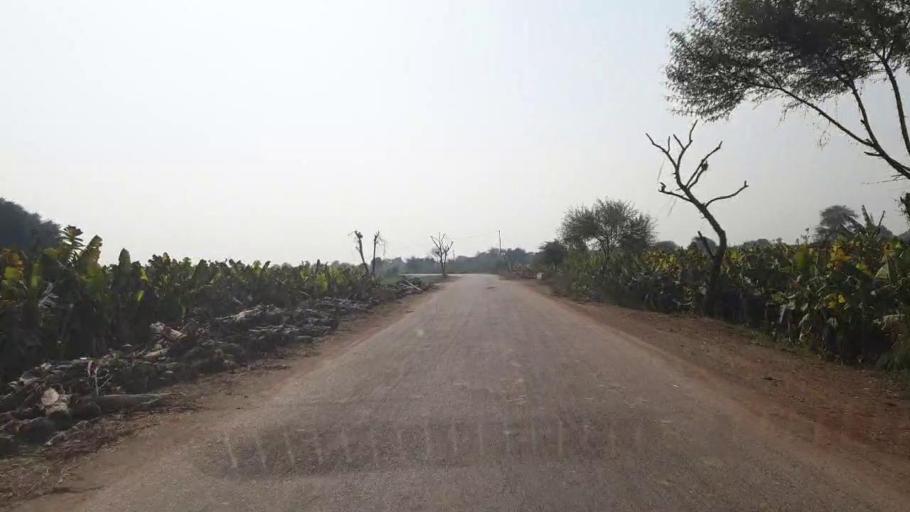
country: PK
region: Sindh
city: Hala
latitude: 25.8651
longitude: 68.4288
